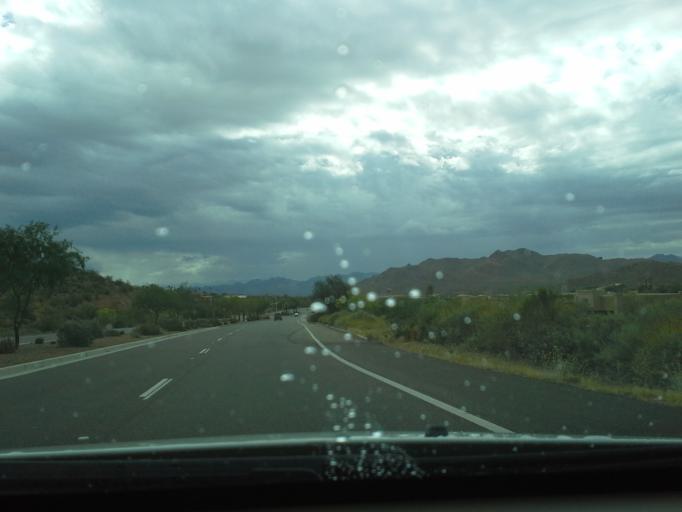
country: US
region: Arizona
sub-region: Maricopa County
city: Fountain Hills
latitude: 33.5777
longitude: -111.7244
